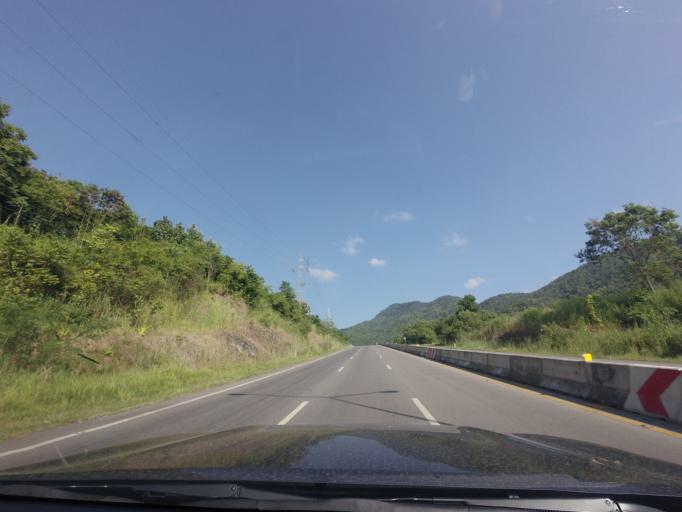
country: TH
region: Phetchabun
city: Lom Sak
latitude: 16.7680
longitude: 101.1374
